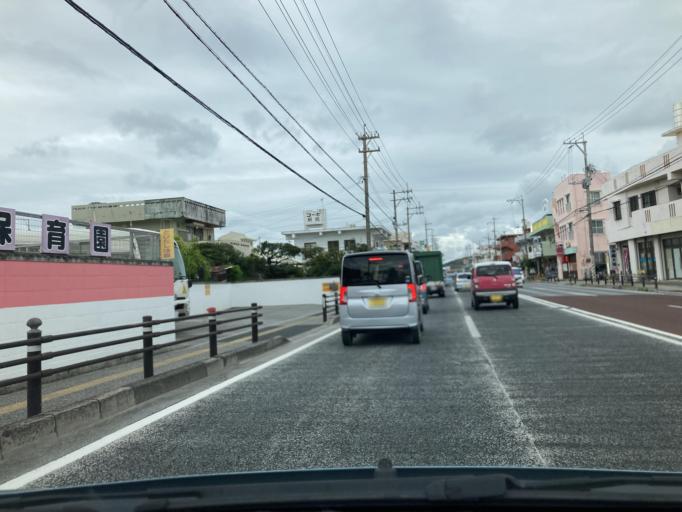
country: JP
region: Okinawa
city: Tomigusuku
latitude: 26.2009
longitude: 127.7436
